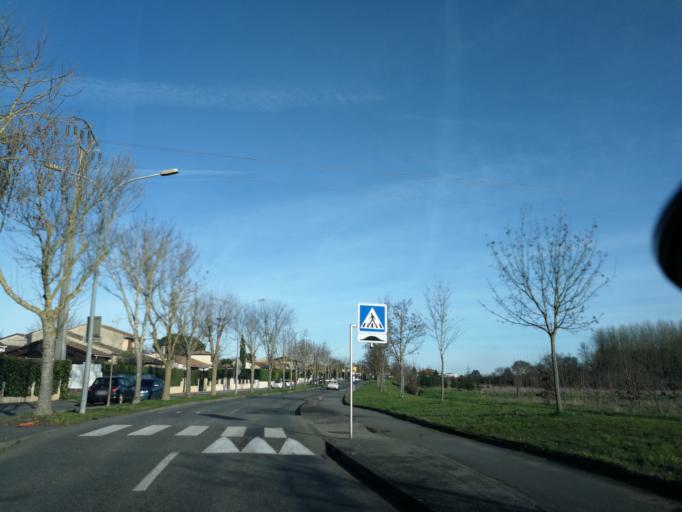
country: FR
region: Midi-Pyrenees
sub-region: Departement de la Haute-Garonne
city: L'Union
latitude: 43.6486
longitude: 1.4920
